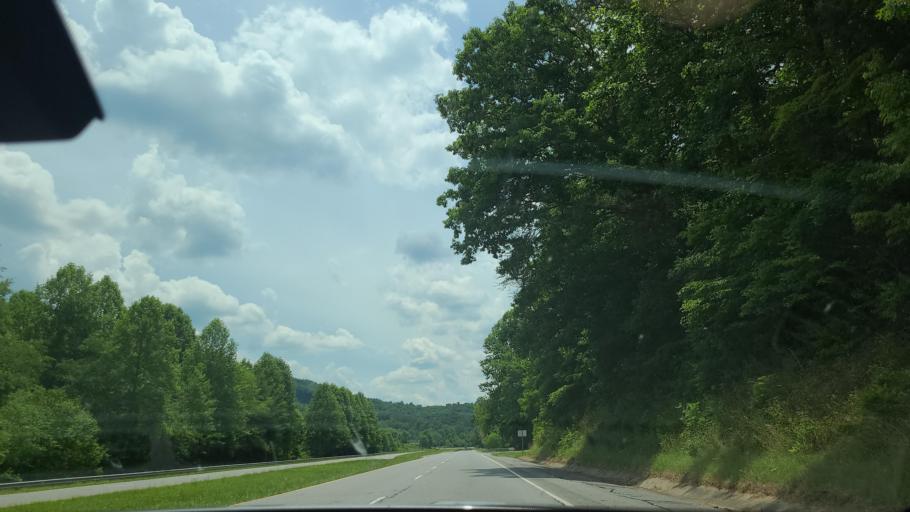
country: US
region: Georgia
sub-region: Fannin County
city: McCaysville
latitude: 35.0296
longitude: -84.2123
